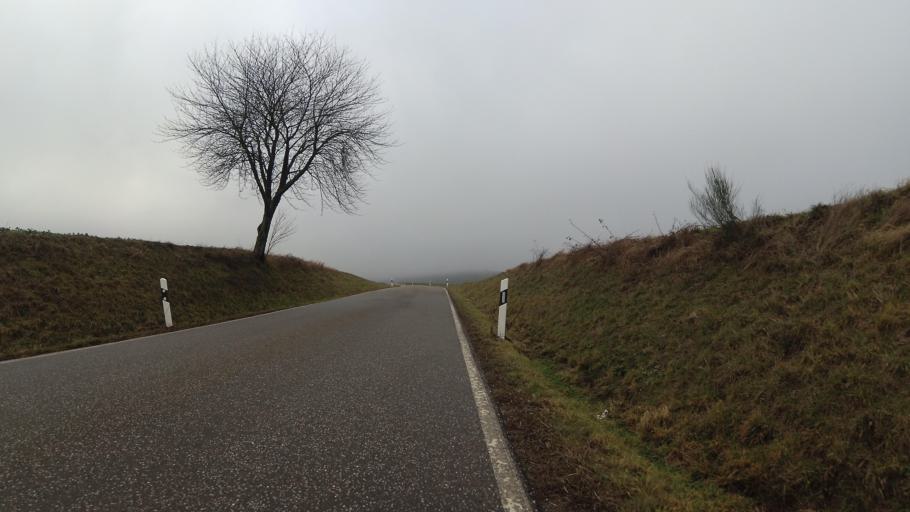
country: DE
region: Rheinland-Pfalz
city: Konken
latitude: 49.5196
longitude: 7.3481
